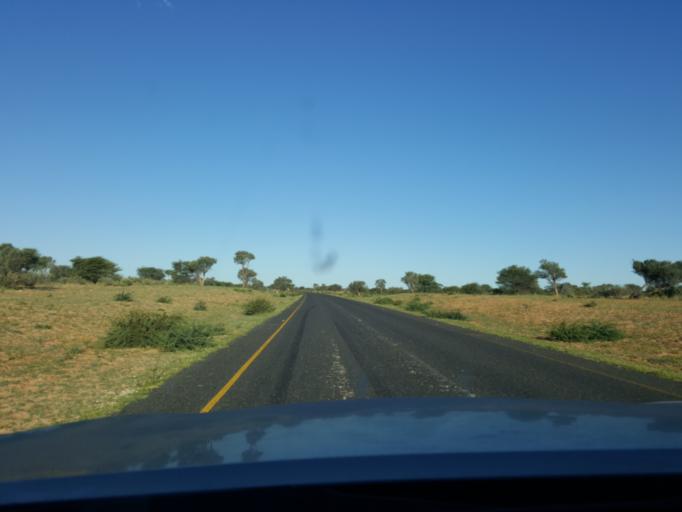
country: BW
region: Southern
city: Khakhea
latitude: -24.2535
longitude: 23.2980
